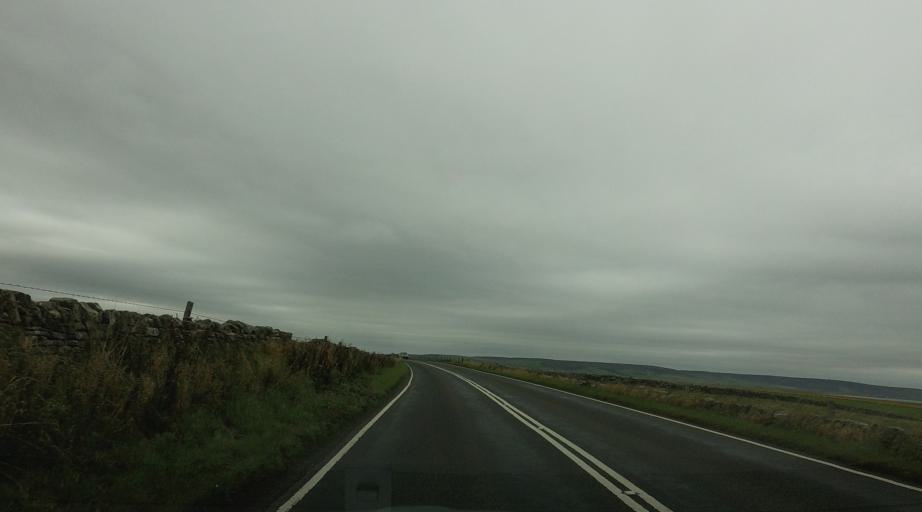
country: GB
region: Scotland
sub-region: Orkney Islands
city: Orkney
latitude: 59.0029
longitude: -3.0033
